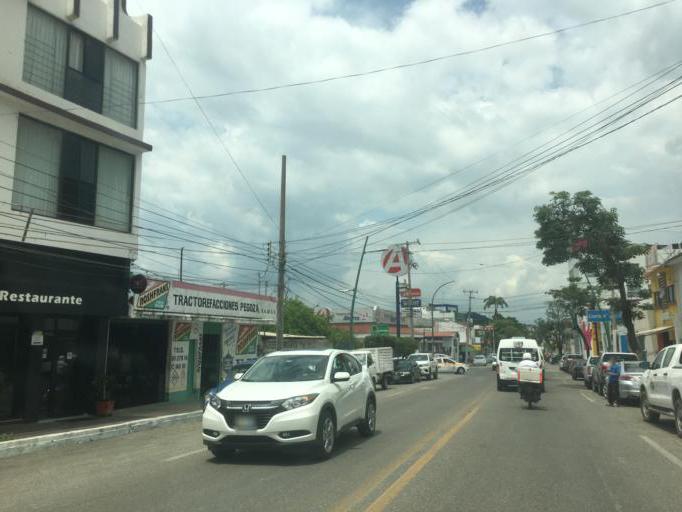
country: MX
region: Chiapas
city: Tuxtla Gutierrez
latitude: 16.7502
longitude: -93.1390
